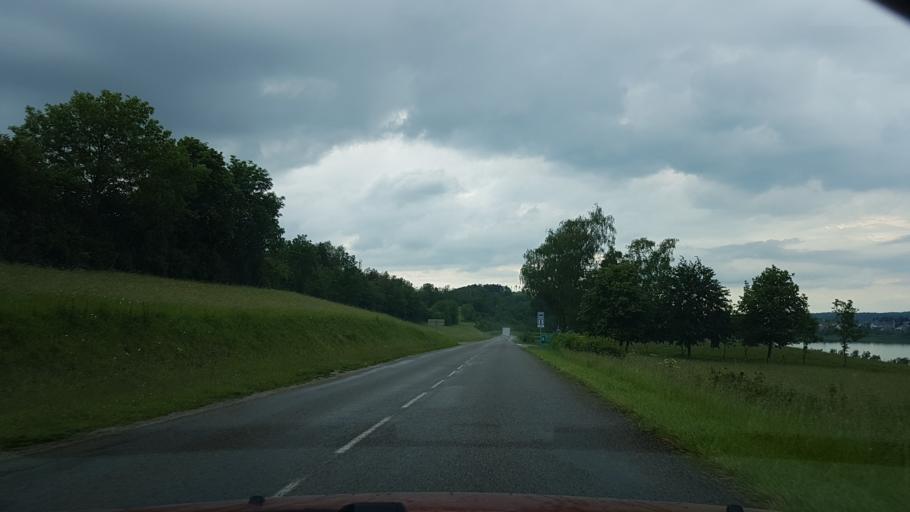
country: FR
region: Franche-Comte
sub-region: Departement du Jura
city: Clairvaux-les-Lacs
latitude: 46.5592
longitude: 5.7449
